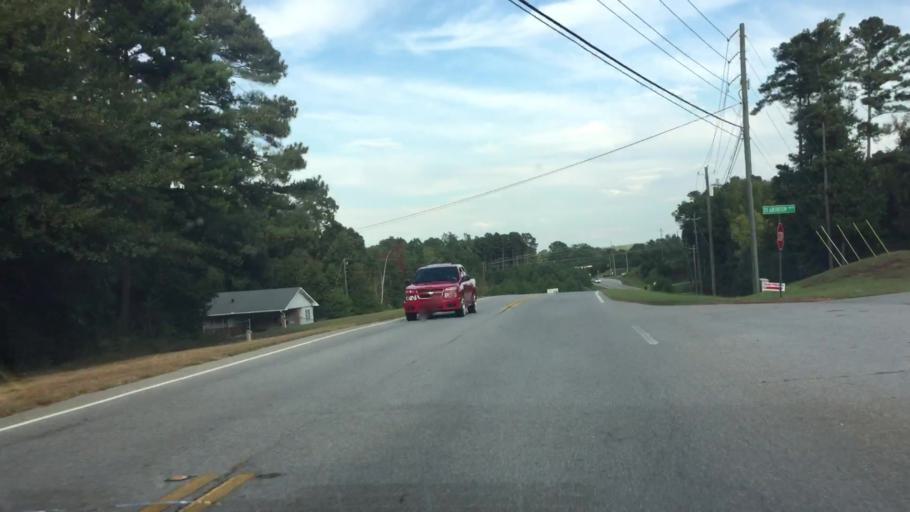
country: US
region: Georgia
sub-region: Henry County
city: McDonough
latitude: 33.5316
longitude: -84.1440
